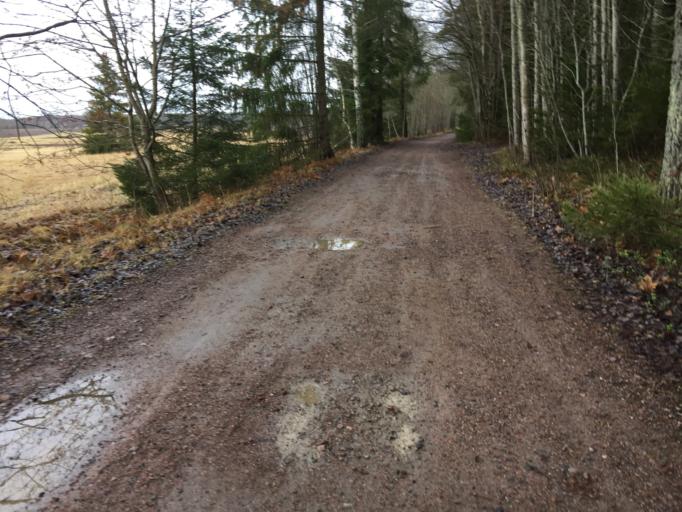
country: SE
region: Uppsala
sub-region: Osthammars Kommun
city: Bjorklinge
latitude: 60.0436
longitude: 17.5429
